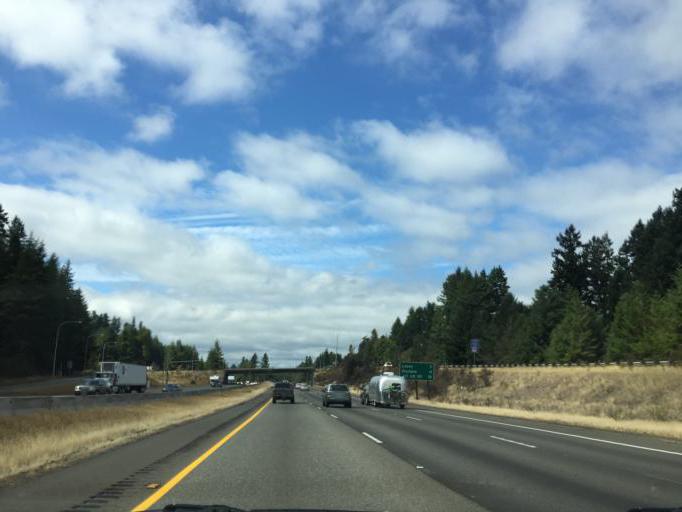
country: US
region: Washington
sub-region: Pierce County
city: DuPont
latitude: 47.0833
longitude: -122.6665
